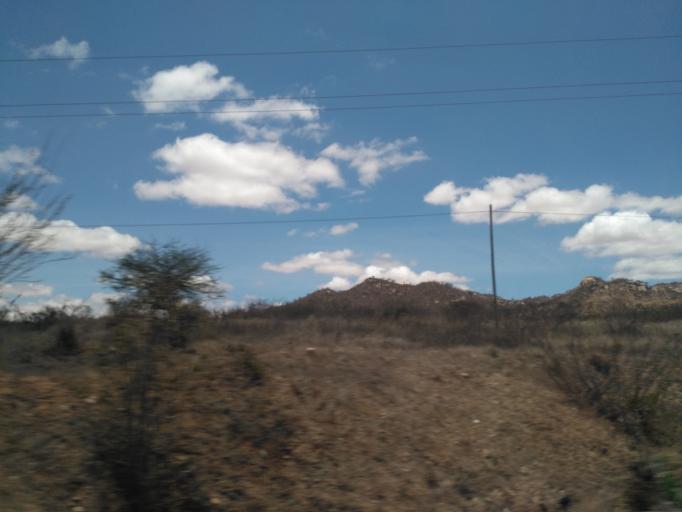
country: TZ
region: Dodoma
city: Kisasa
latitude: -6.2192
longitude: 35.8093
